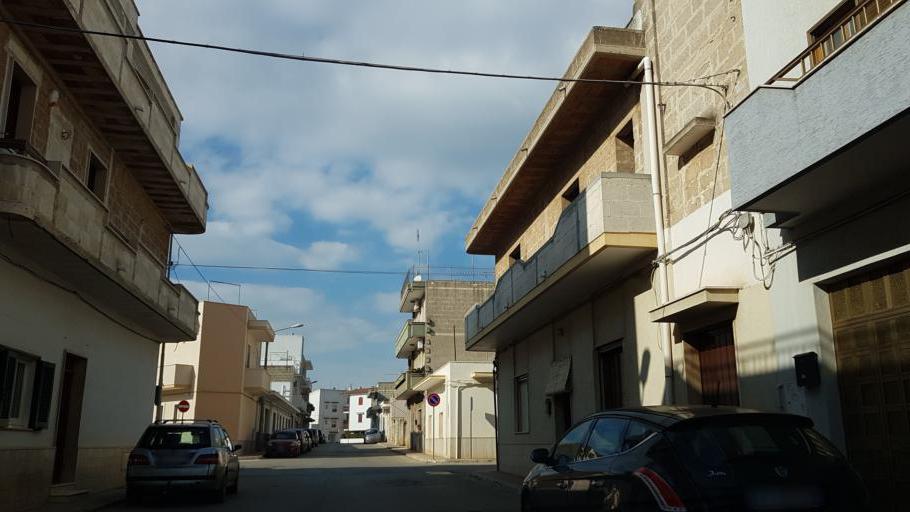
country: IT
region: Apulia
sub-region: Provincia di Brindisi
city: Carovigno
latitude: 40.7106
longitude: 17.6631
